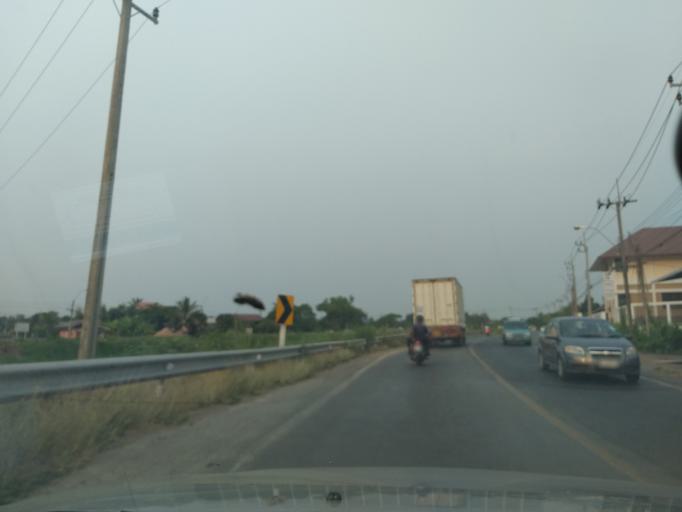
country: TH
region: Bangkok
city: Nong Chok
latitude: 13.8604
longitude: 100.8698
